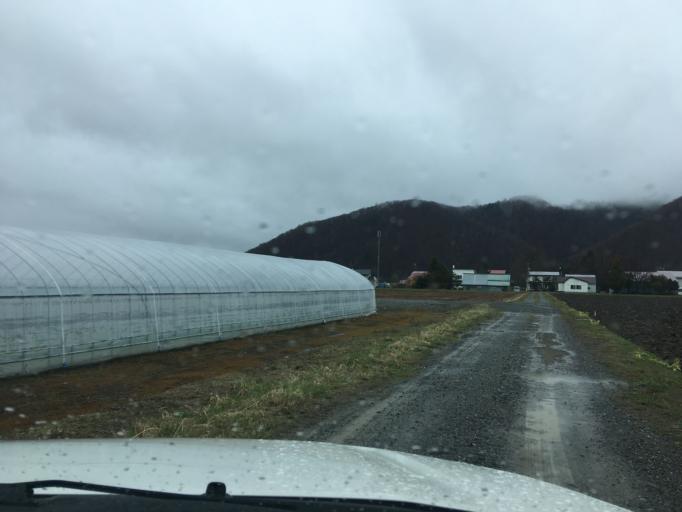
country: JP
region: Hokkaido
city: Nayoro
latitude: 44.1329
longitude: 142.4896
